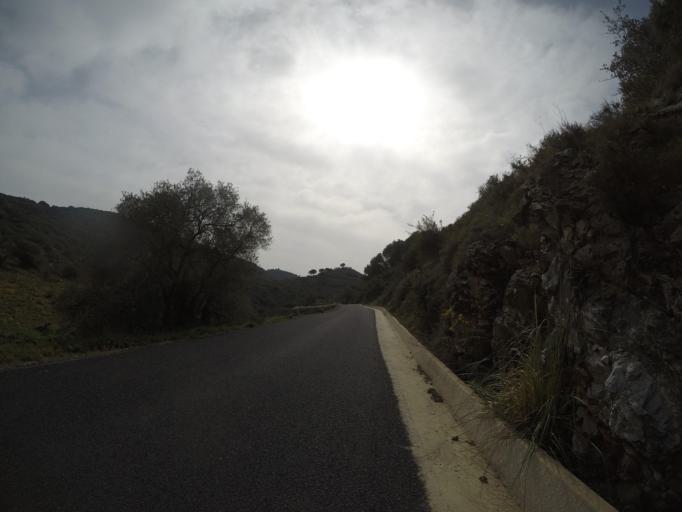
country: FR
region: Languedoc-Roussillon
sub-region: Departement des Pyrenees-Orientales
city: Estagel
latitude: 42.7697
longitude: 2.7025
